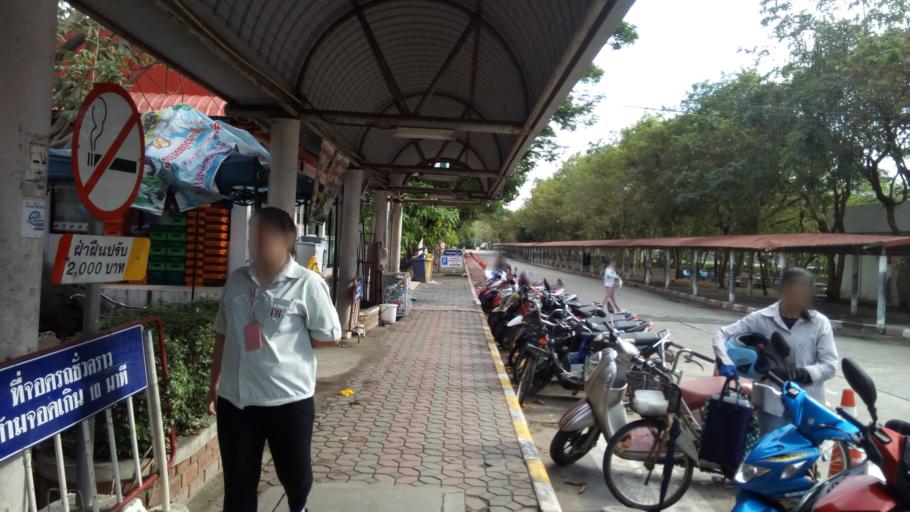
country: TH
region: Nakhon Nayok
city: Ongkharak
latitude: 14.1117
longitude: 100.9855
